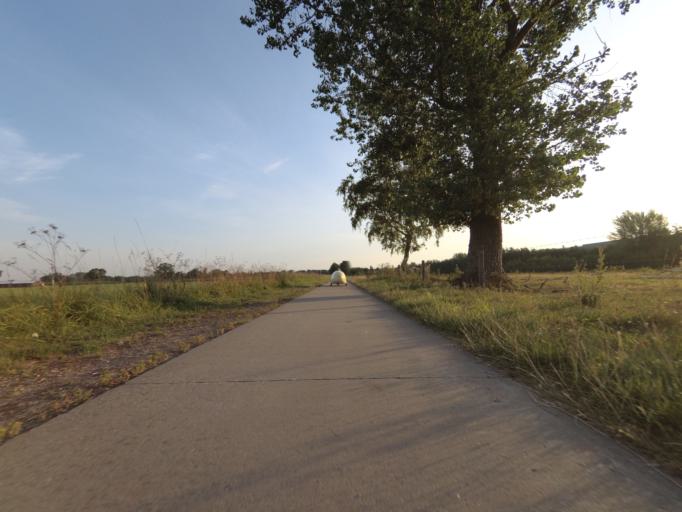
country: NL
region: Overijssel
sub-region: Gemeente Hof van Twente
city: Markelo
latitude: 52.3173
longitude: 6.4925
